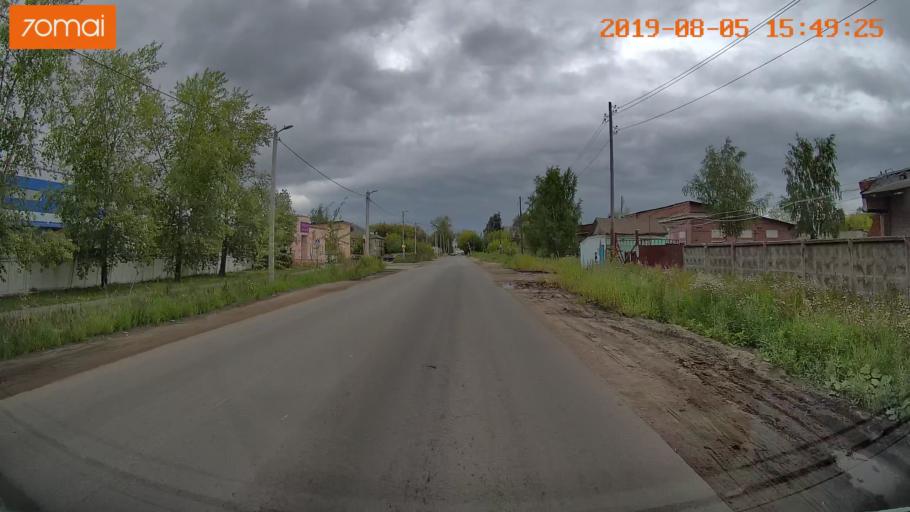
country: RU
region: Ivanovo
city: Novo-Talitsy
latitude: 56.9940
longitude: 40.9116
